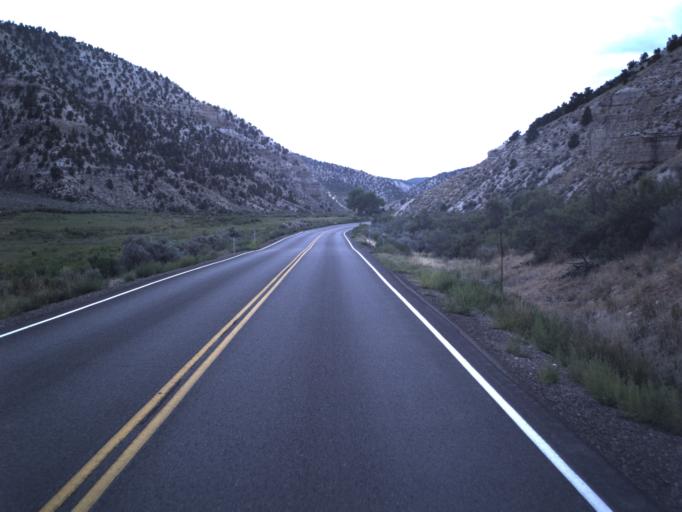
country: US
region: Utah
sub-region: Duchesne County
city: Duchesne
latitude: 40.0946
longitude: -110.4860
